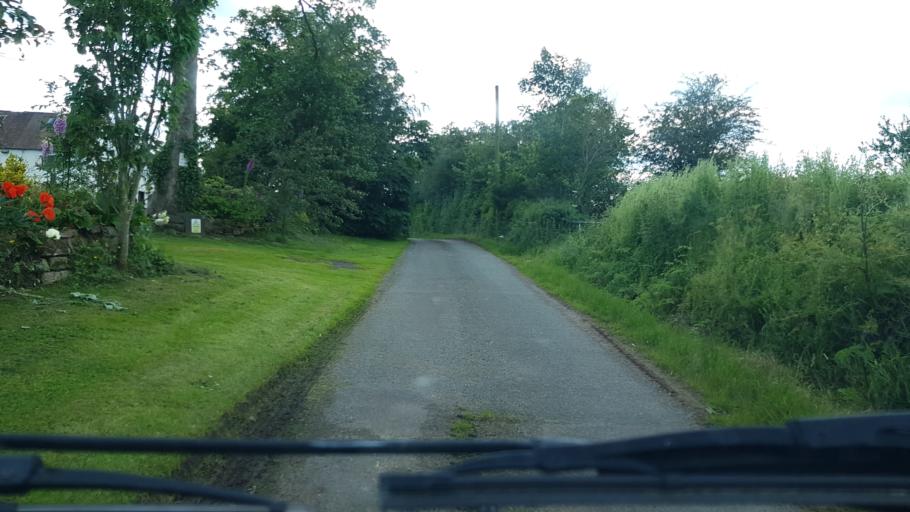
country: GB
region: England
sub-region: Shropshire
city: Romsley
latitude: 52.4501
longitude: -2.3049
